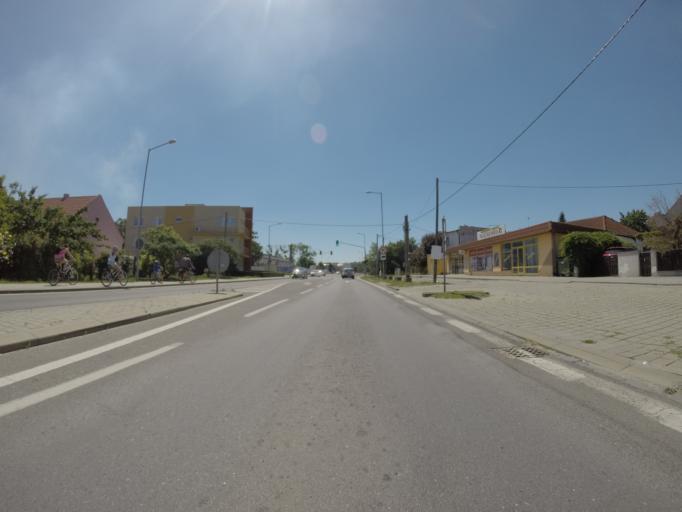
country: SK
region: Trnavsky
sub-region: Okres Galanta
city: Galanta
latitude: 48.1977
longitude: 17.7332
